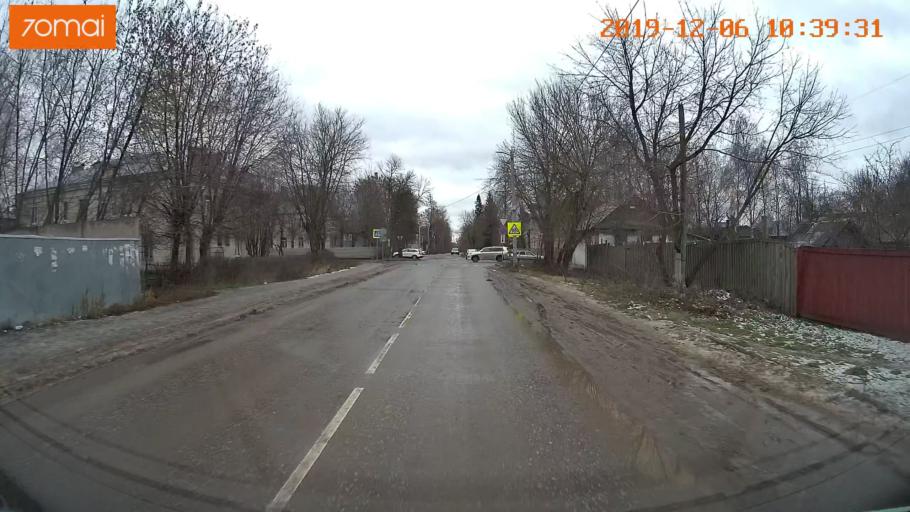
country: RU
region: Ivanovo
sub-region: Gorod Ivanovo
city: Ivanovo
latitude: 57.0308
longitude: 40.9749
